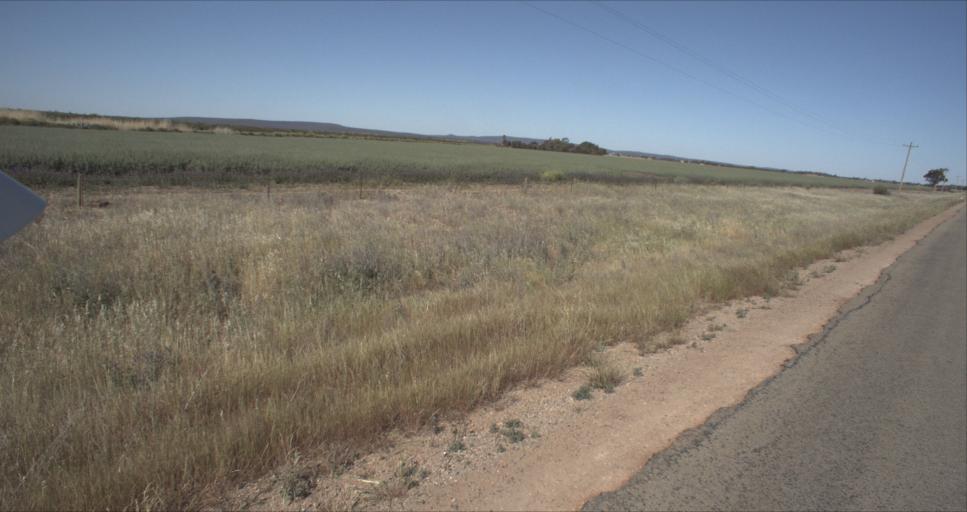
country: AU
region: New South Wales
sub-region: Leeton
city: Leeton
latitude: -34.4808
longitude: 146.3711
